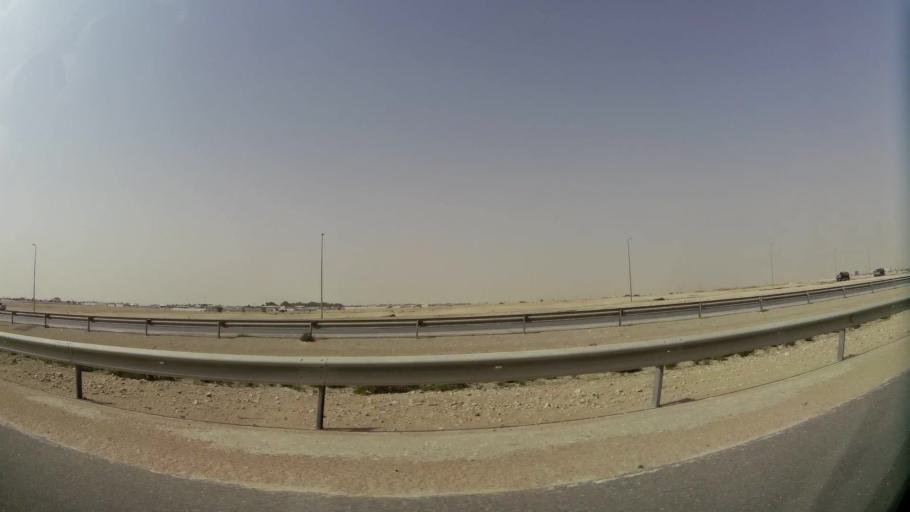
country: QA
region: Baladiyat ar Rayyan
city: Ar Rayyan
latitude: 25.1645
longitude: 51.3051
